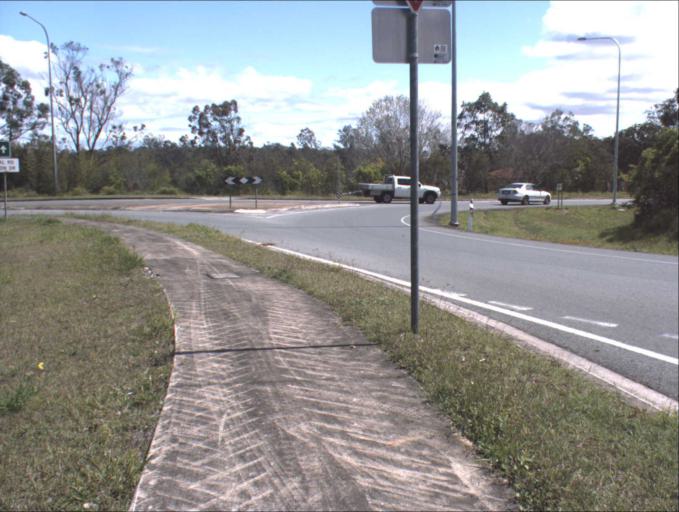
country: AU
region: Queensland
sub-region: Logan
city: Park Ridge South
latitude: -27.7256
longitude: 153.0291
